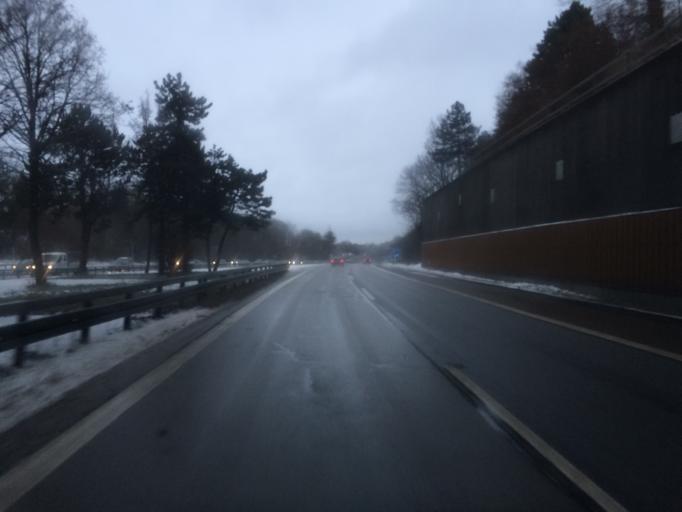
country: DE
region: Bavaria
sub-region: Upper Palatinate
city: Lappersdorf
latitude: 49.0367
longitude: 12.0883
